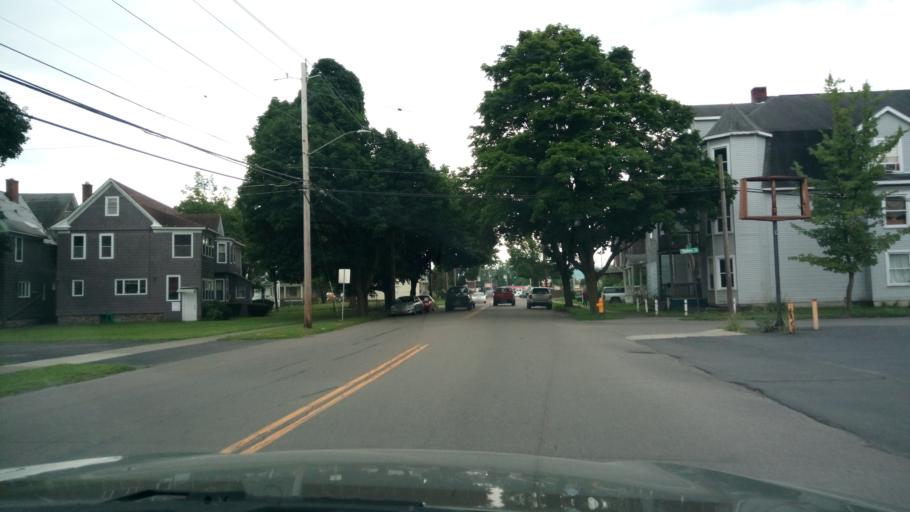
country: US
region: New York
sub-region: Chemung County
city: Elmira
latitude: 42.1035
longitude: -76.8048
